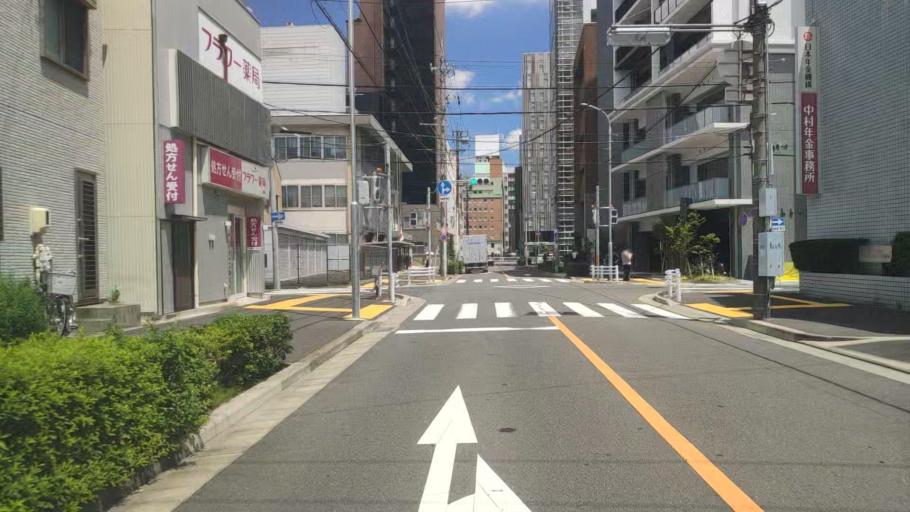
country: JP
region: Aichi
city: Nagoya-shi
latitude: 35.1664
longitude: 136.8803
